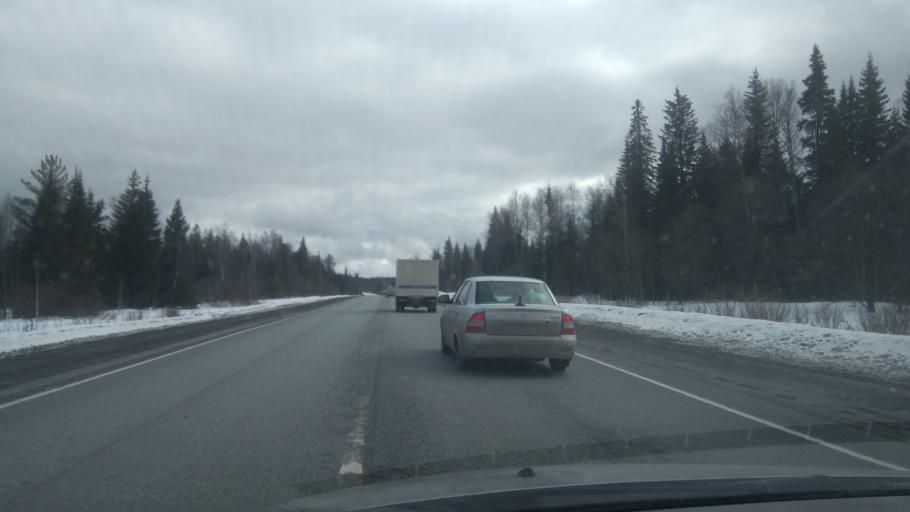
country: RU
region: Sverdlovsk
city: Atig
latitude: 56.8108
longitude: 59.3634
